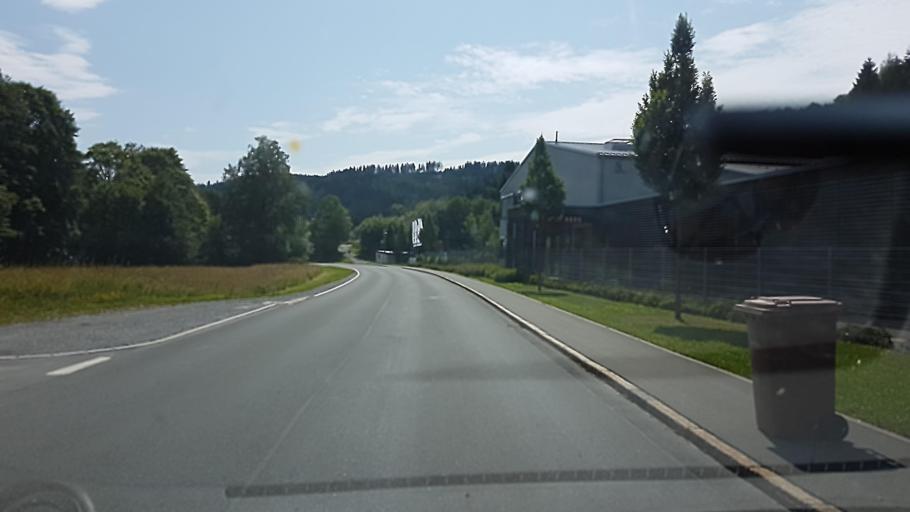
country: DE
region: Bavaria
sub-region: Upper Franconia
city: Warmensteinach
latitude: 49.9915
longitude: 11.7771
